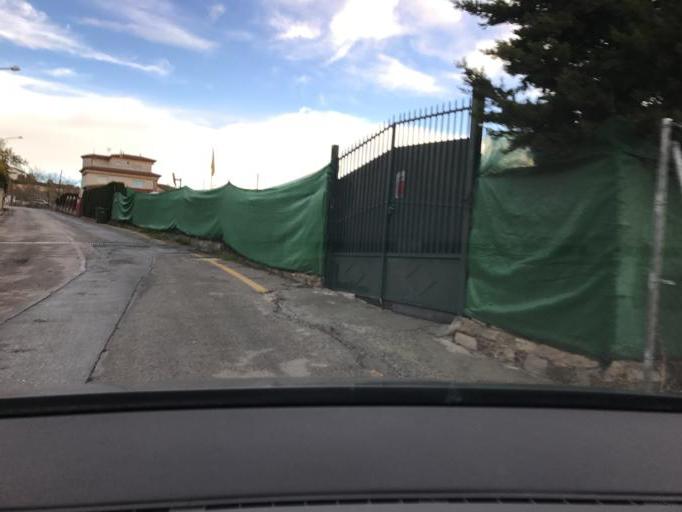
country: ES
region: Andalusia
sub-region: Provincia de Granada
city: Cenes de la Vega
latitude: 37.1625
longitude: -3.5384
